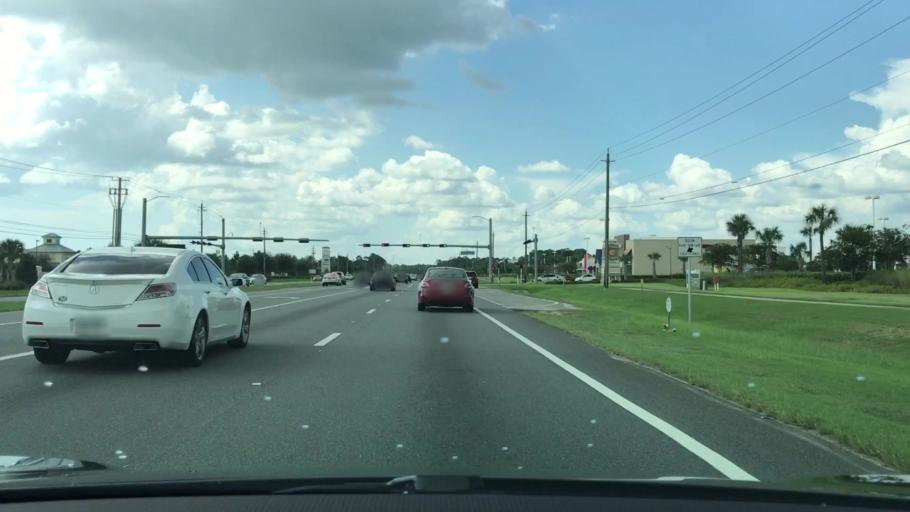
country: US
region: Florida
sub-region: Bay County
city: Laguna Beach
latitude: 30.2202
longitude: -85.8647
